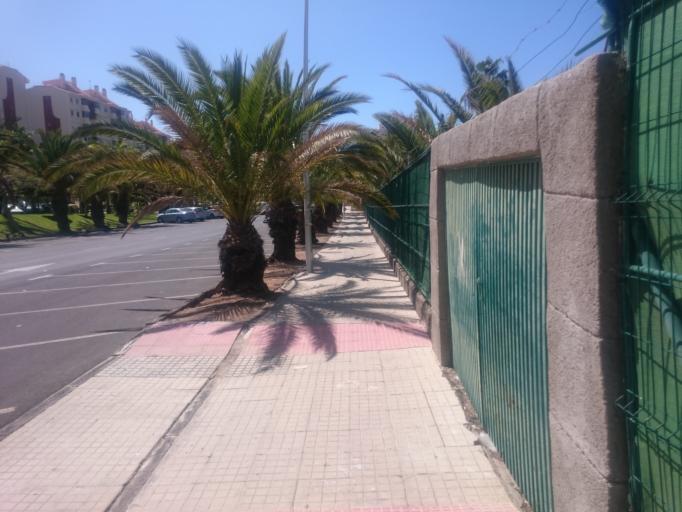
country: ES
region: Canary Islands
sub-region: Provincia de Santa Cruz de Tenerife
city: Playa de las Americas
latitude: 28.0505
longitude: -16.7098
